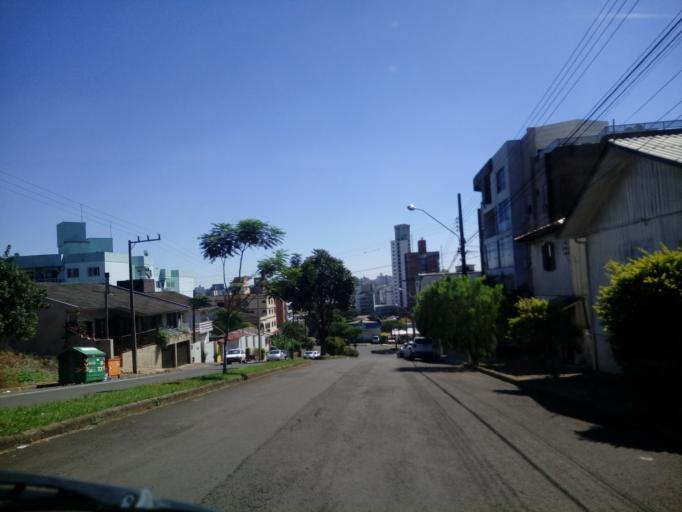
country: BR
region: Santa Catarina
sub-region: Chapeco
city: Chapeco
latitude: -27.1047
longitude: -52.6237
